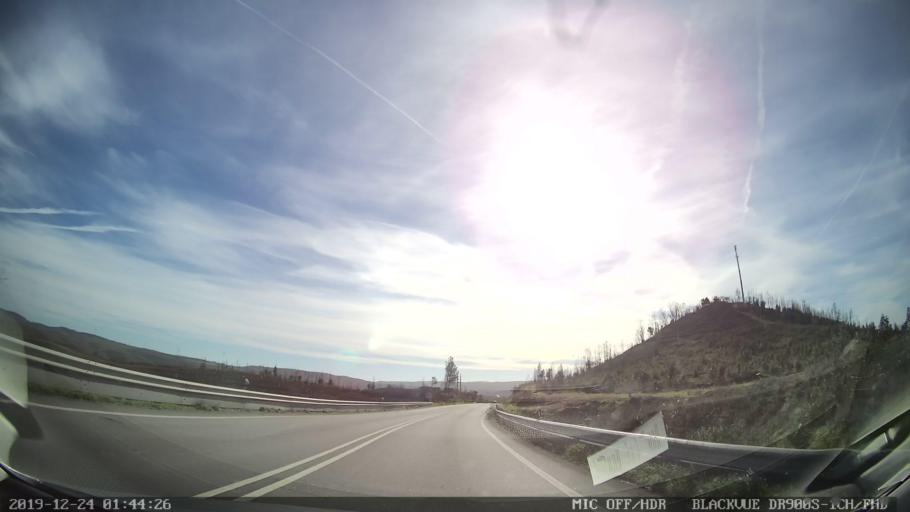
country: PT
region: Portalegre
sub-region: Nisa
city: Nisa
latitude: 39.5550
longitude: -7.7939
